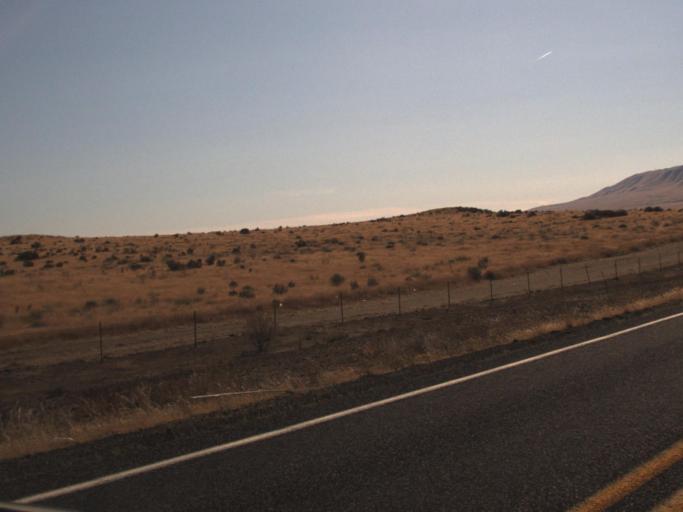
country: US
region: Washington
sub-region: Grant County
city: Desert Aire
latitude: 46.5737
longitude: -119.7277
